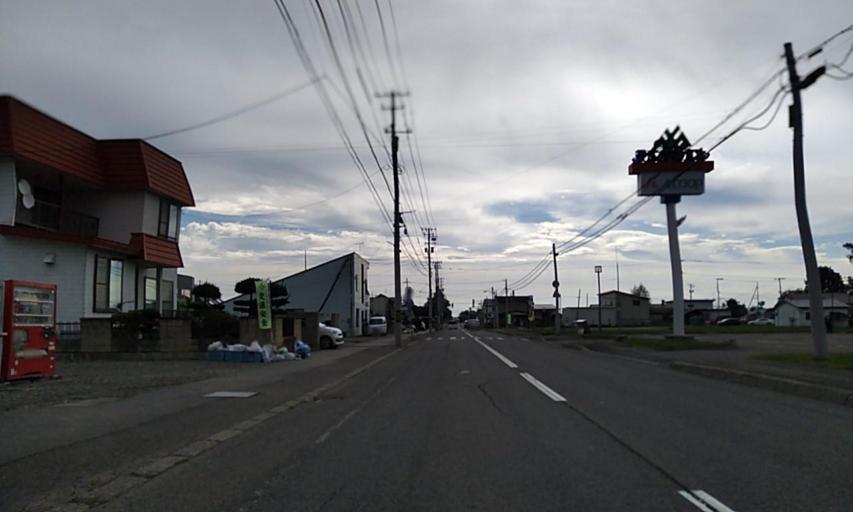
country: JP
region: Hokkaido
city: Obihiro
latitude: 42.8494
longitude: 143.1658
